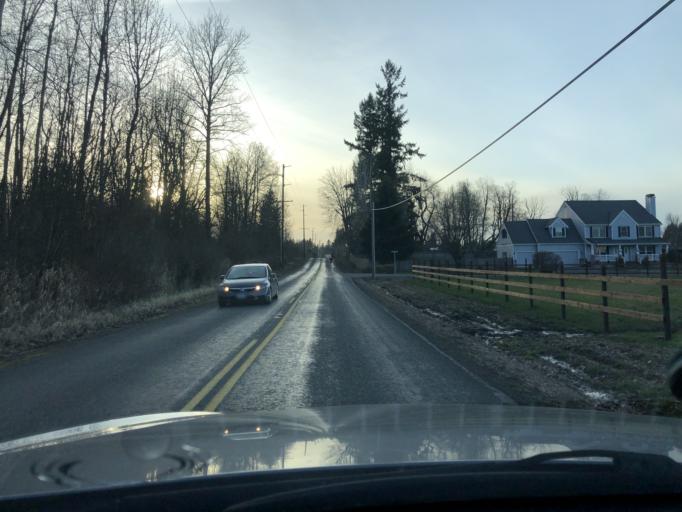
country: US
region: Washington
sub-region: Pierce County
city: Bonney Lake
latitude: 47.2211
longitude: -122.1295
